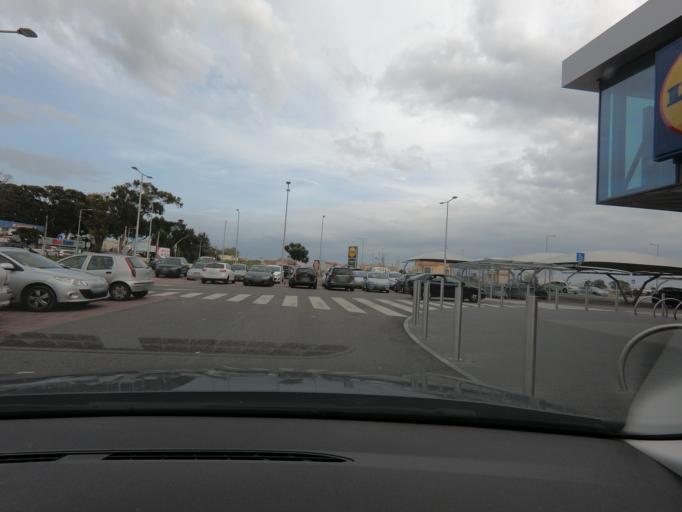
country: PT
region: Lisbon
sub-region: Cascais
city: Sao Domingos de Rana
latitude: 38.7285
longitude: -9.3359
